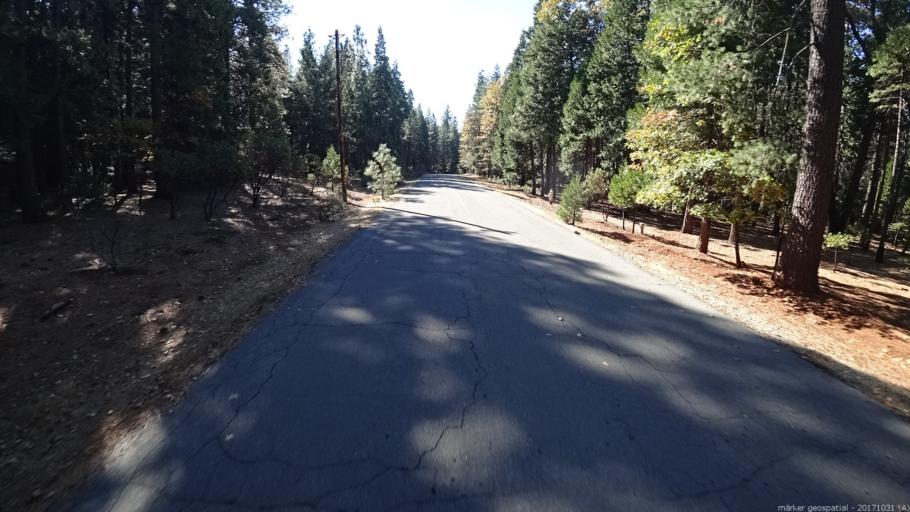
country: US
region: California
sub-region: Shasta County
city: Shingletown
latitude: 40.4863
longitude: -121.8889
